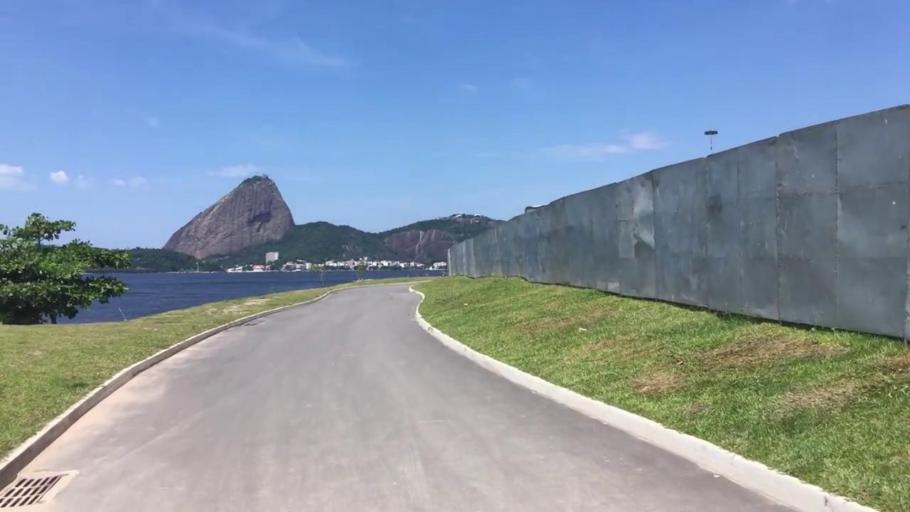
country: BR
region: Rio de Janeiro
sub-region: Rio De Janeiro
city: Rio de Janeiro
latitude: -22.9194
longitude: -43.1681
